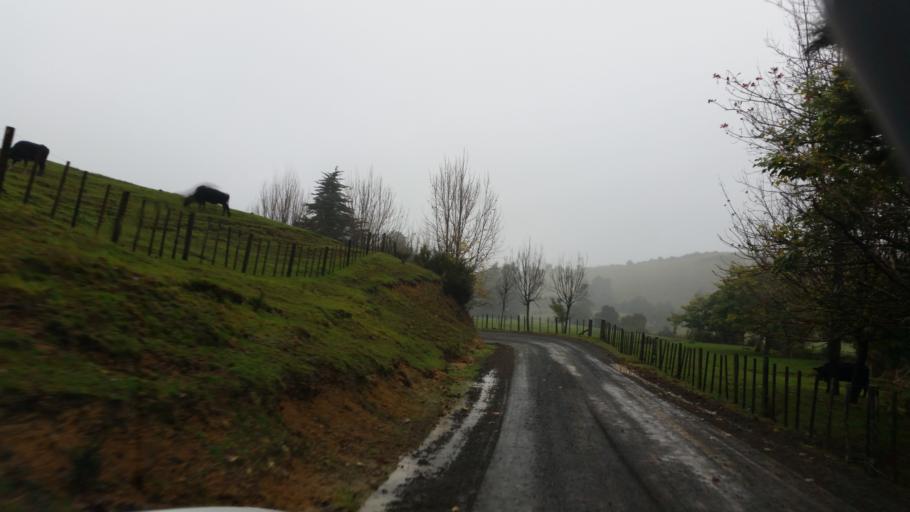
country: NZ
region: Northland
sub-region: Whangarei
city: Ngunguru
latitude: -35.4944
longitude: 174.4268
